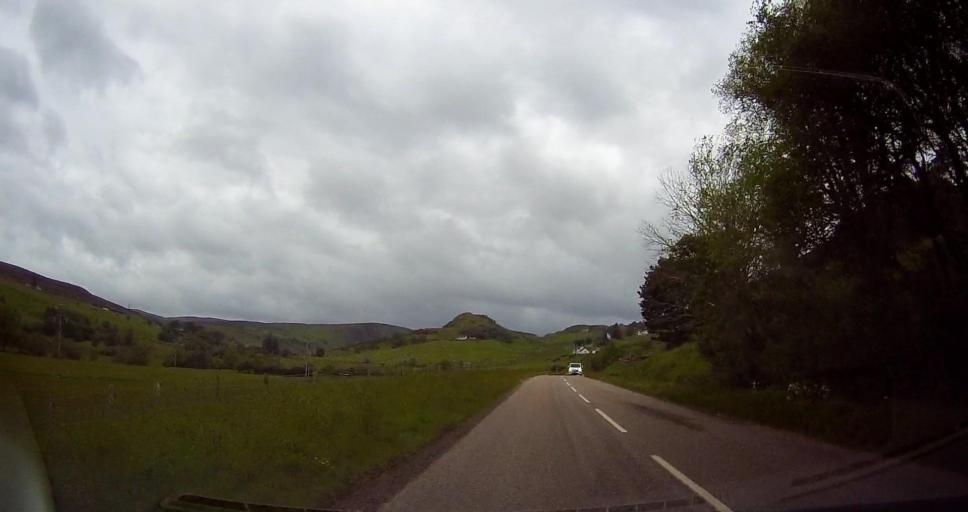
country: GB
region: Scotland
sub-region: Highland
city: Dornoch
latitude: 58.0065
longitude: -4.2393
